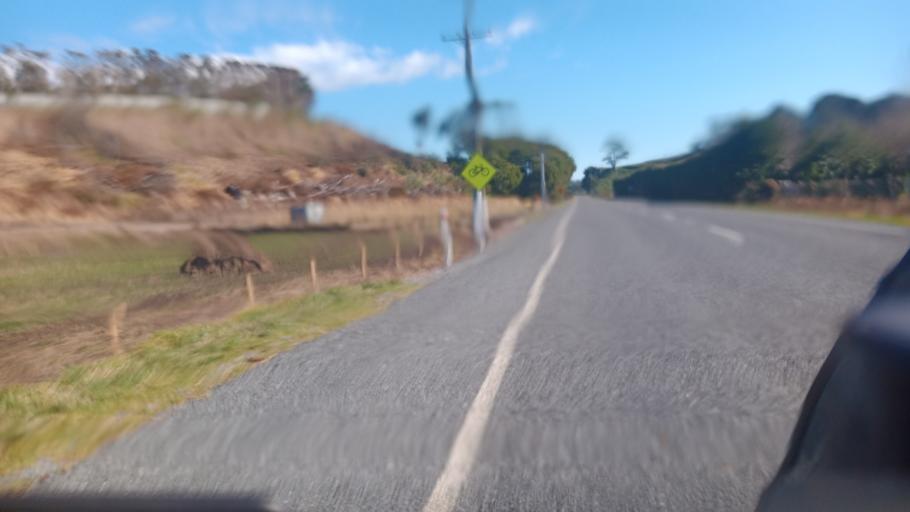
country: NZ
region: Bay of Plenty
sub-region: Opotiki District
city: Opotiki
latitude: -37.9890
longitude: 177.3519
